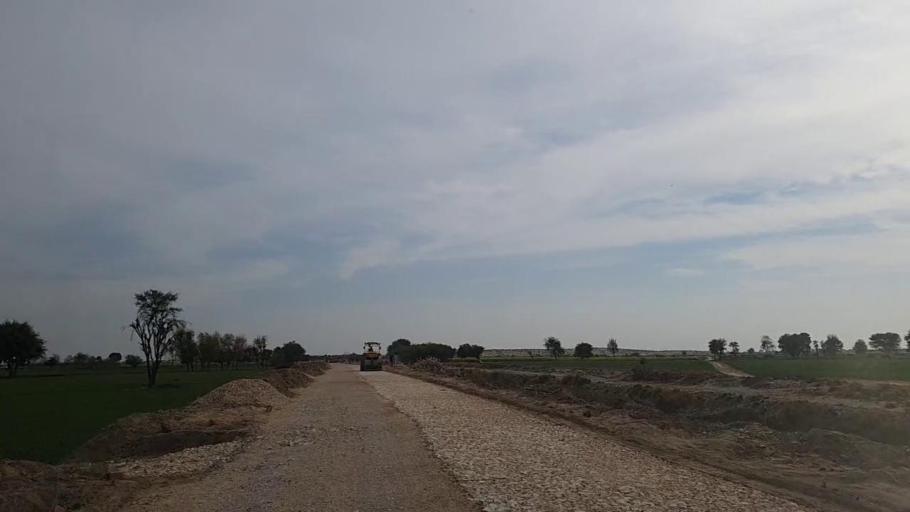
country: PK
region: Sindh
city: Jam Sahib
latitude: 26.4077
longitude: 68.4934
